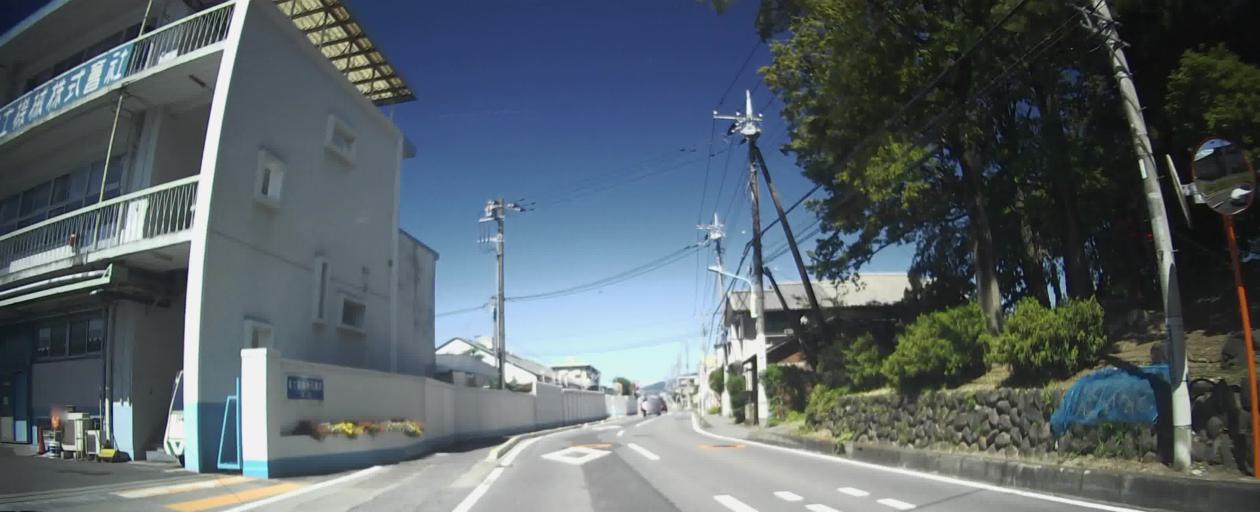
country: JP
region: Gunma
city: Maebashi-shi
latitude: 36.4014
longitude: 139.0556
